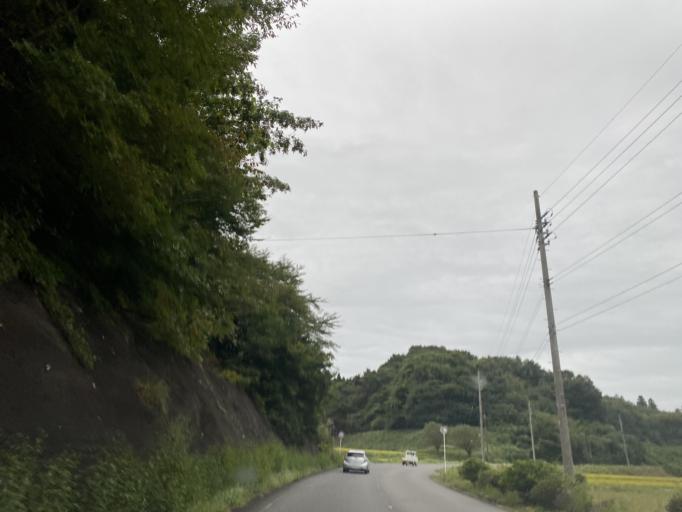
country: JP
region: Fukushima
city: Sukagawa
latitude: 37.3016
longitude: 140.2533
